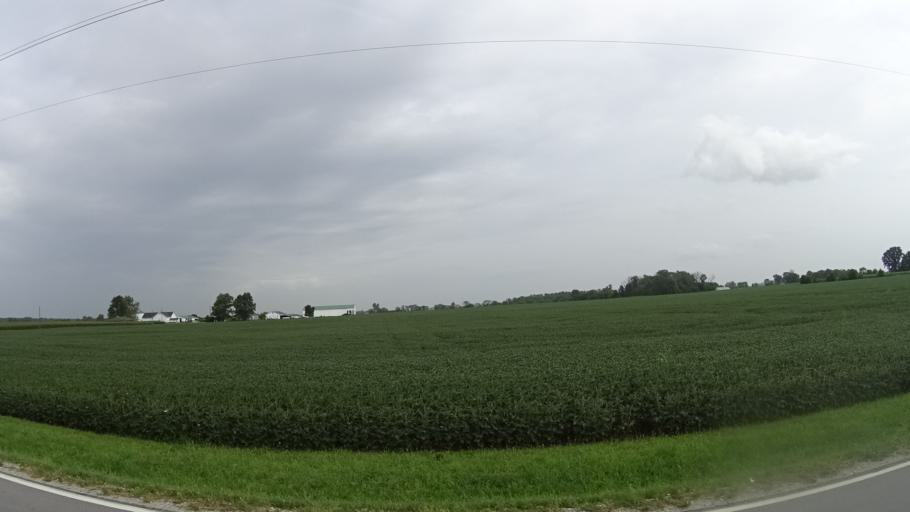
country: US
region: Indiana
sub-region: Madison County
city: Lapel
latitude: 40.0178
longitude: -85.8326
